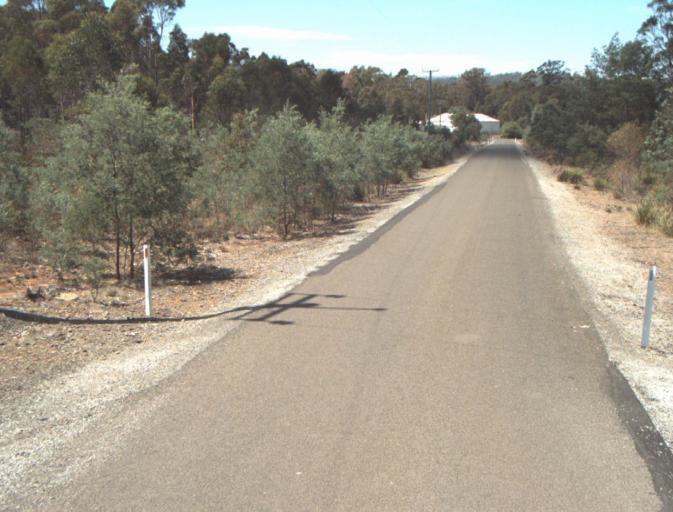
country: AU
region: Tasmania
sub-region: Launceston
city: Mayfield
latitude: -41.3248
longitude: 147.1299
